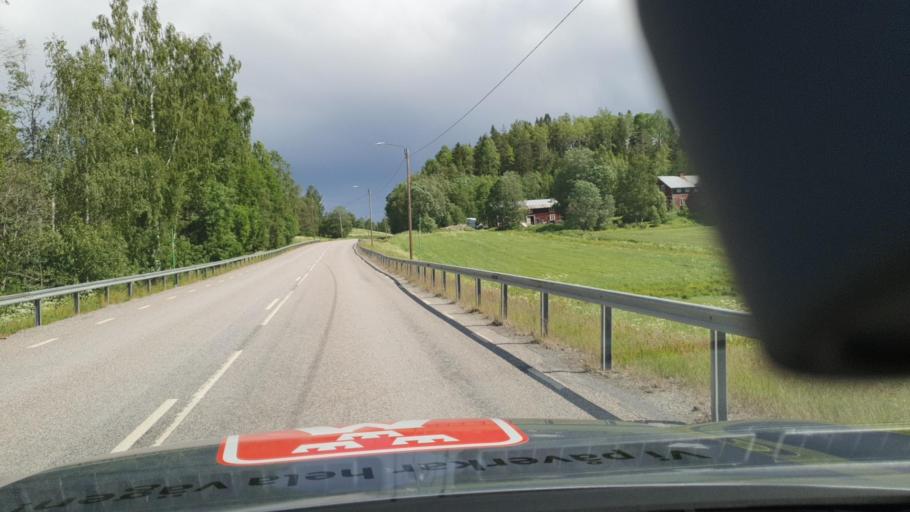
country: SE
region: Vaesternorrland
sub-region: OErnskoeldsviks Kommun
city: Bjasta
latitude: 63.2491
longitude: 18.3966
